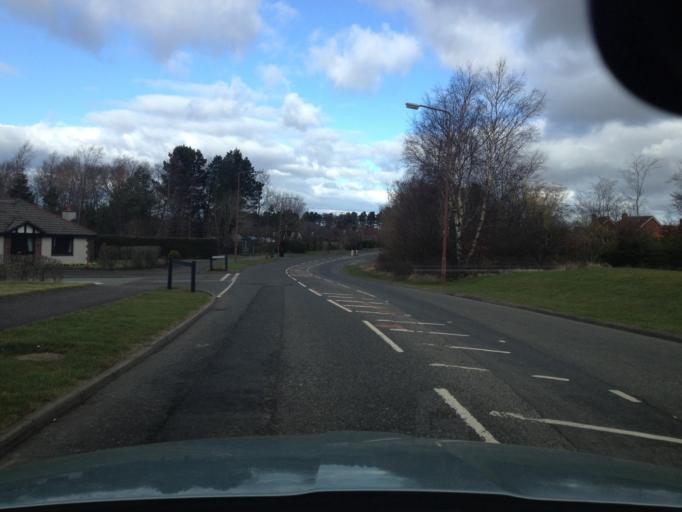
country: GB
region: Scotland
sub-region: West Lothian
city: Mid Calder
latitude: 55.8603
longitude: -3.5088
